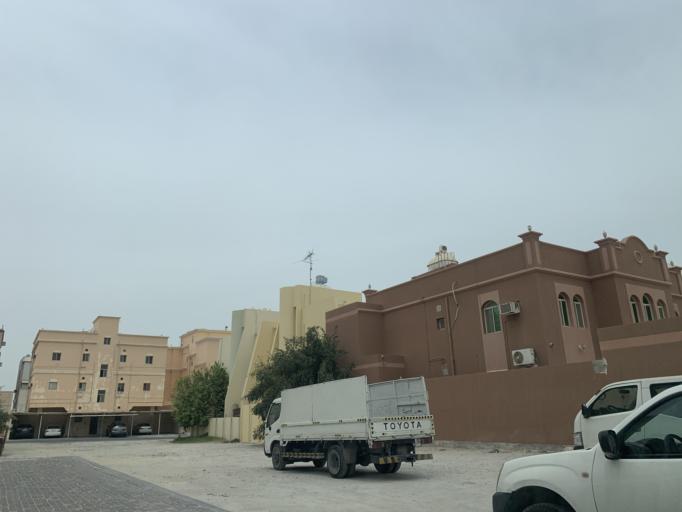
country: BH
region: Northern
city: Ar Rifa'
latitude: 26.1315
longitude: 50.5644
